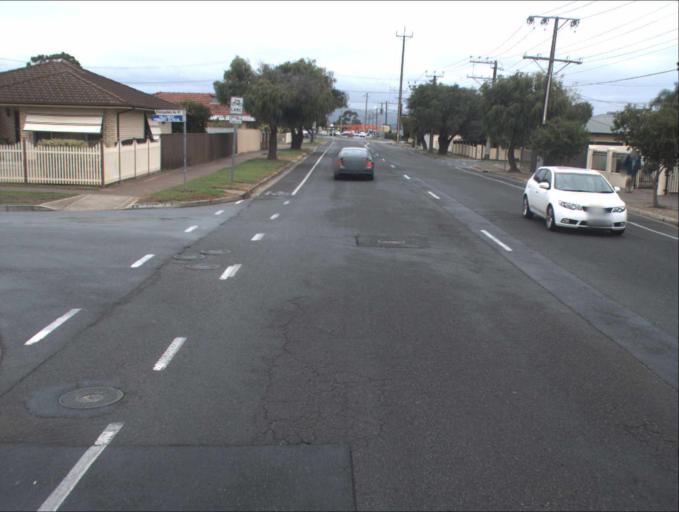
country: AU
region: South Australia
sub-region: Port Adelaide Enfield
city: Klemzig
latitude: -34.8675
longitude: 138.6369
